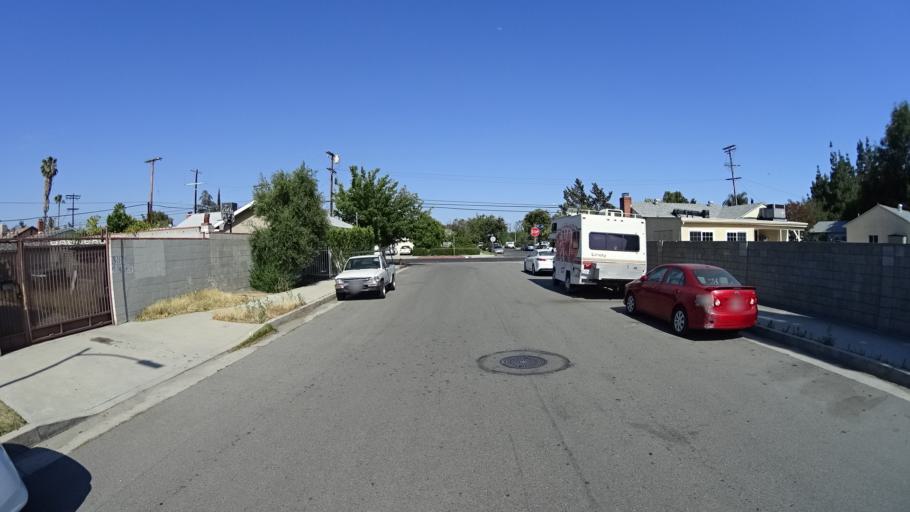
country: US
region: California
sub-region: Los Angeles County
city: Van Nuys
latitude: 34.2091
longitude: -118.4182
